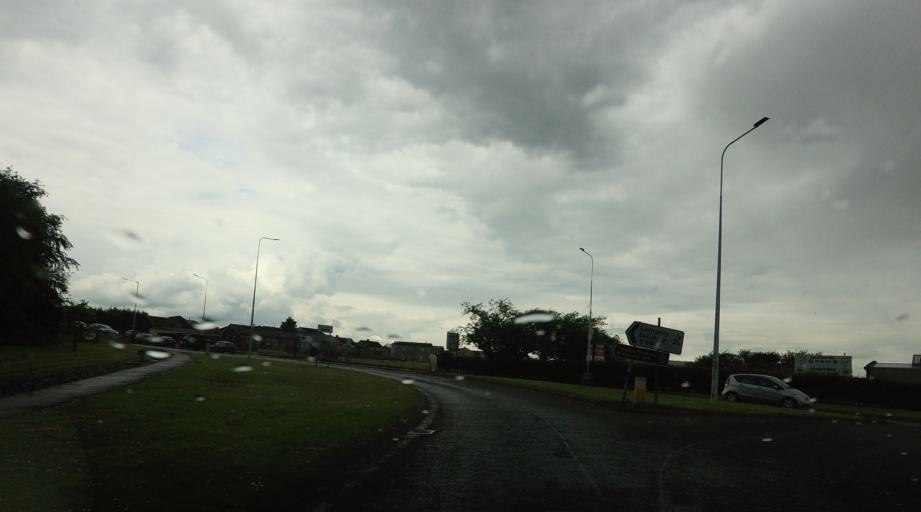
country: GB
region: Scotland
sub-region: Fife
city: Lochgelly
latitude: 56.1316
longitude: -3.3020
